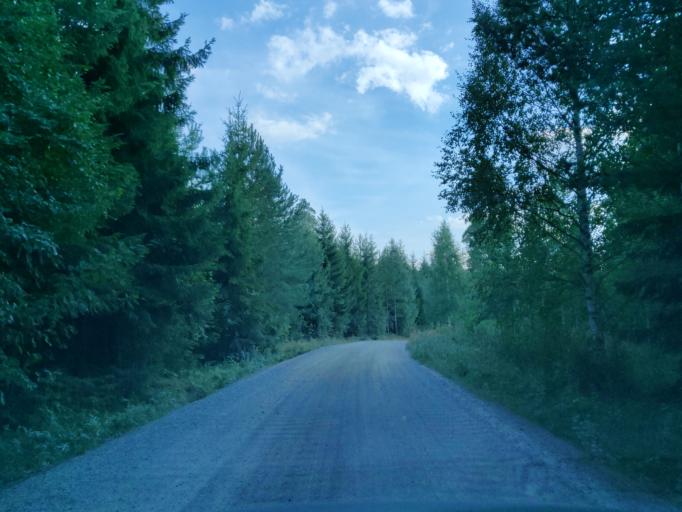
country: SE
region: Vaermland
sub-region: Hagfors Kommun
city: Hagfors
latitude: 60.0166
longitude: 13.6754
